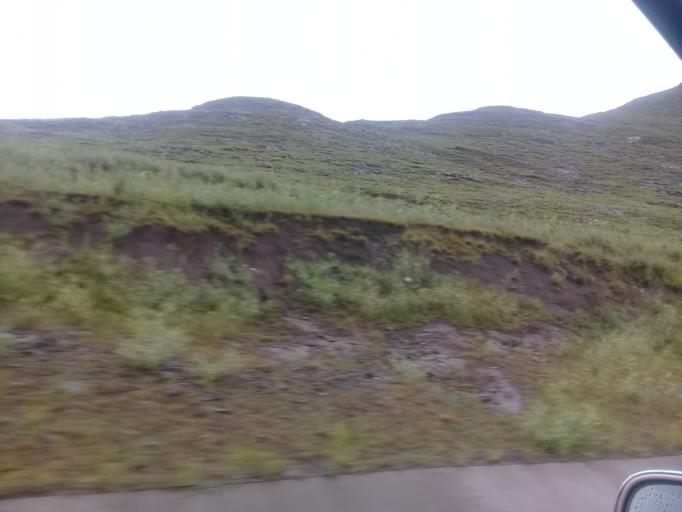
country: LS
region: Mokhotlong
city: Mokhotlong
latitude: -29.3117
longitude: 29.0268
